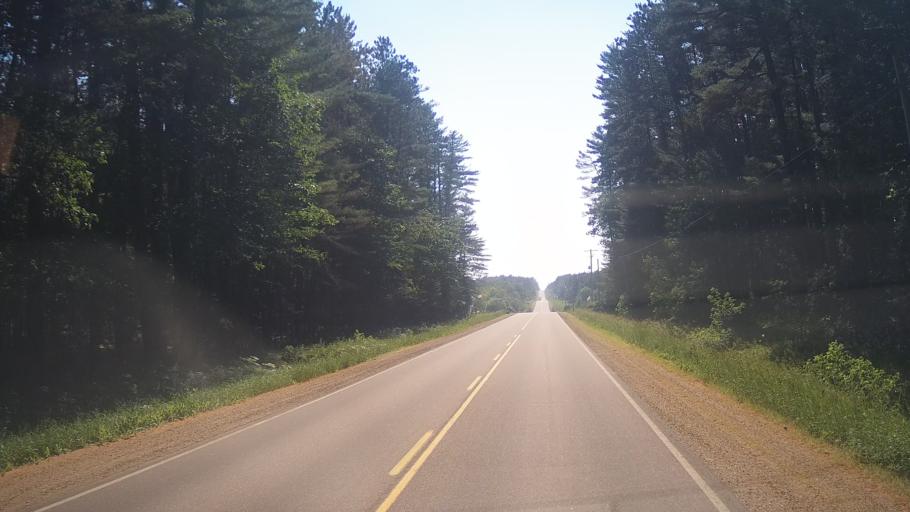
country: CA
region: Ontario
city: Pembroke
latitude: 45.6234
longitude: -77.1524
